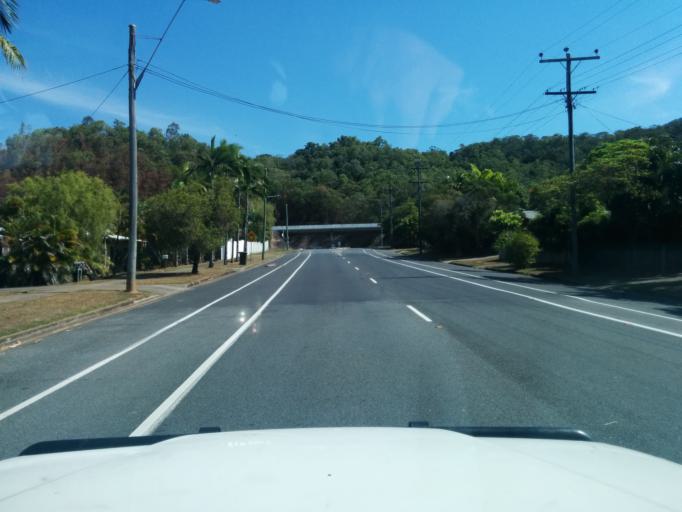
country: AU
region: Queensland
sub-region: Cairns
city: Cairns
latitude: -16.9131
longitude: 145.7279
